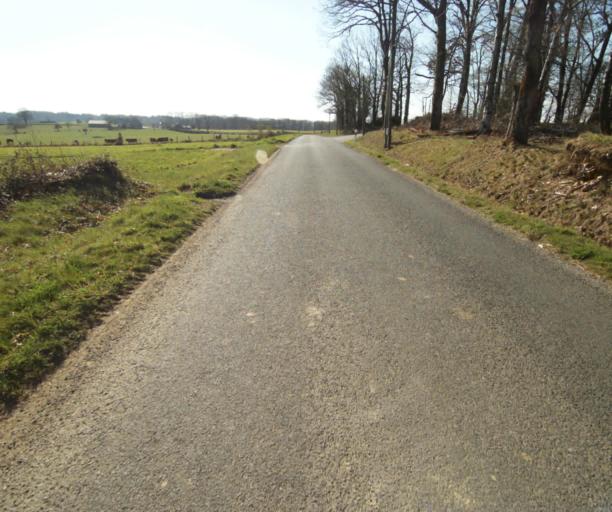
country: FR
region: Limousin
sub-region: Departement de la Correze
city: Chamboulive
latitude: 45.4698
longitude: 1.6915
